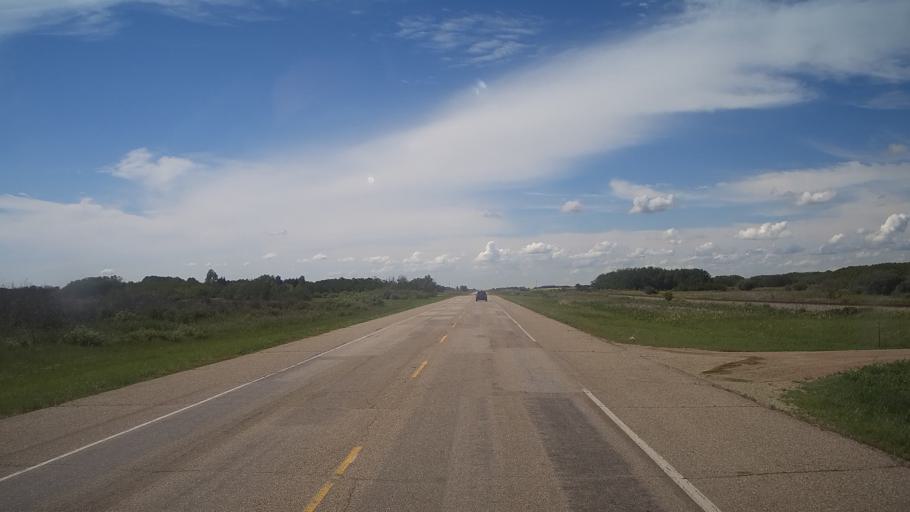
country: CA
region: Saskatchewan
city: Yorkton
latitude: 51.0619
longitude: -102.2073
